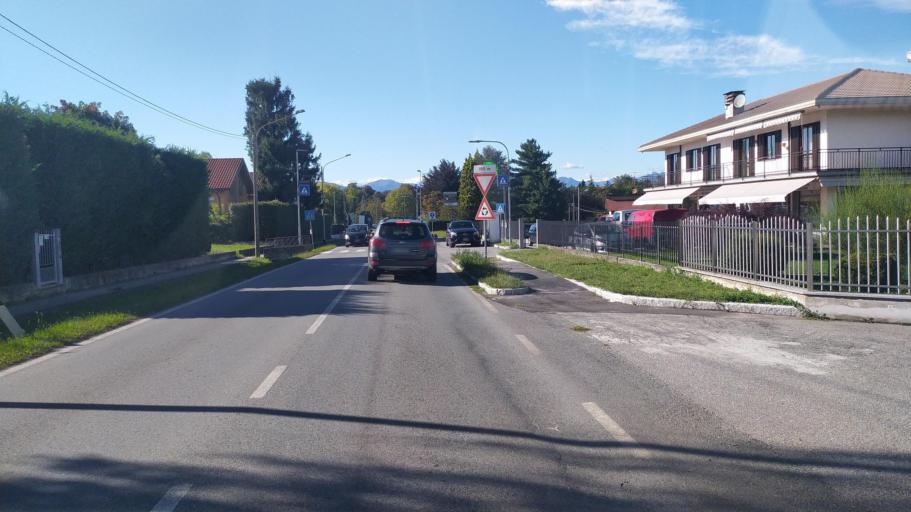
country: IT
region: Lombardy
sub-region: Provincia di Varese
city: Cazzago Brabbia
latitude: 45.7940
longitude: 8.7391
